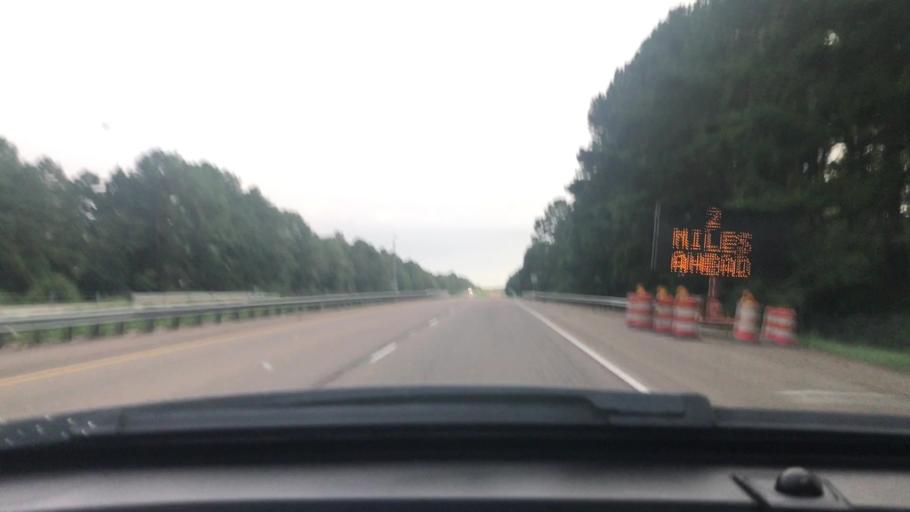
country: US
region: Louisiana
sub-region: Tangipahoa Parish
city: Kentwood
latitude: 30.9960
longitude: -90.5067
